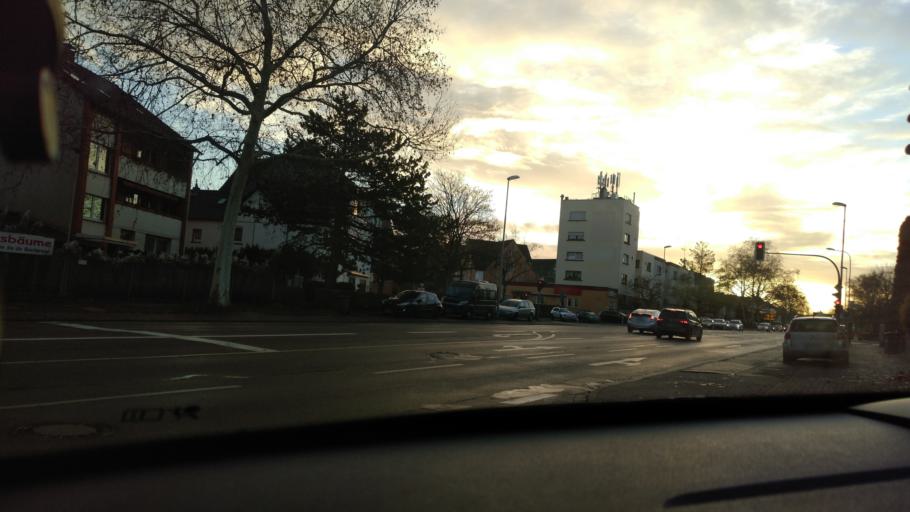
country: DE
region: North Rhine-Westphalia
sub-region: Regierungsbezirk Dusseldorf
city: Muelheim (Ruhr)
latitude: 51.4053
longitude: 6.8710
